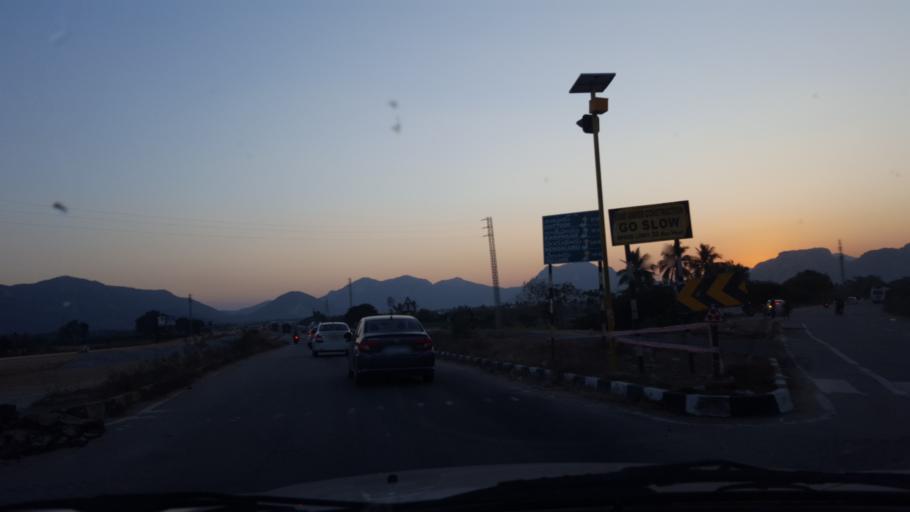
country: IN
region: Andhra Pradesh
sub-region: Chittoor
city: Narasingapuram
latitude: 13.5972
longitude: 79.3499
